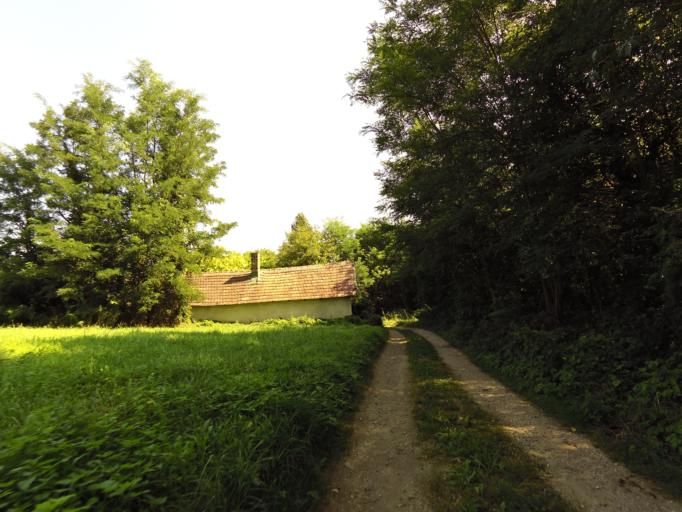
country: HU
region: Zala
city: Vonyarcvashegy
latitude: 46.8324
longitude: 17.3589
